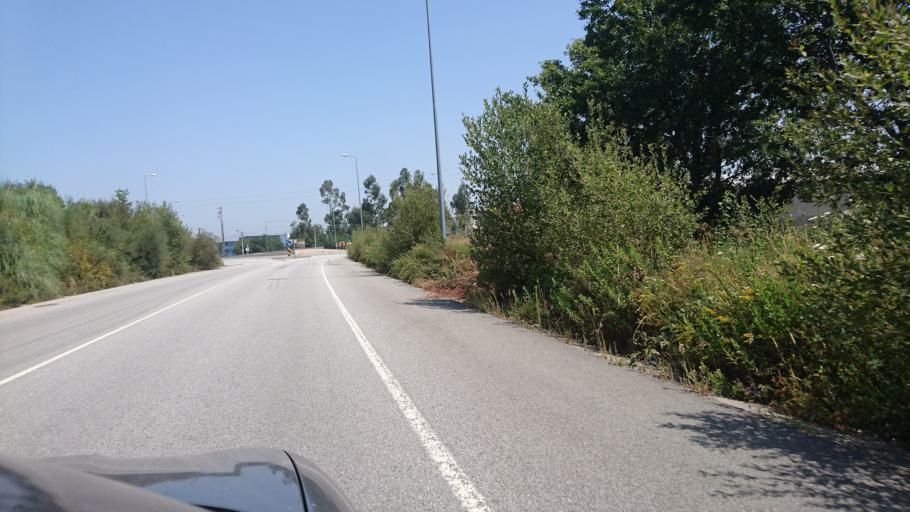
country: PT
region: Porto
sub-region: Valongo
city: Campo
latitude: 41.1703
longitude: -8.4406
